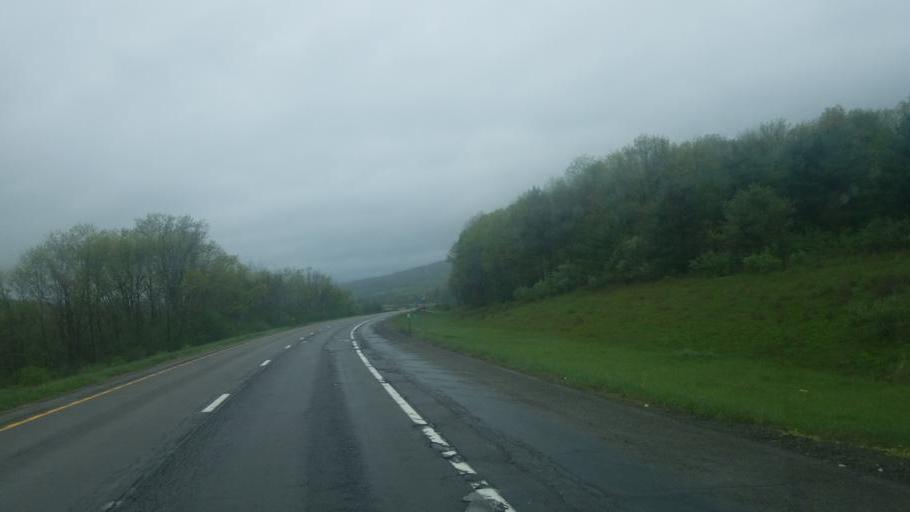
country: US
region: New York
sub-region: Allegany County
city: Belmont
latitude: 42.2977
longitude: -77.9347
